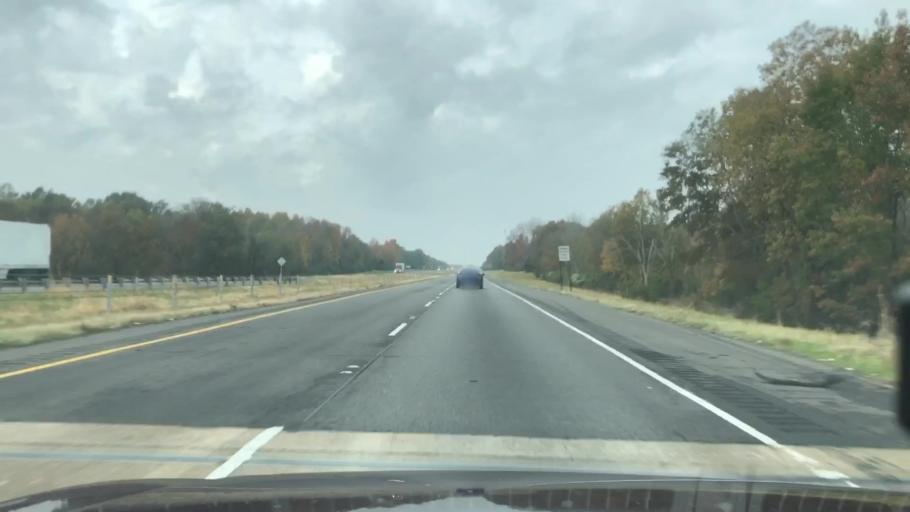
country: US
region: Louisiana
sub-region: Richland Parish
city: Delhi
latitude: 32.4396
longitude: -91.4724
